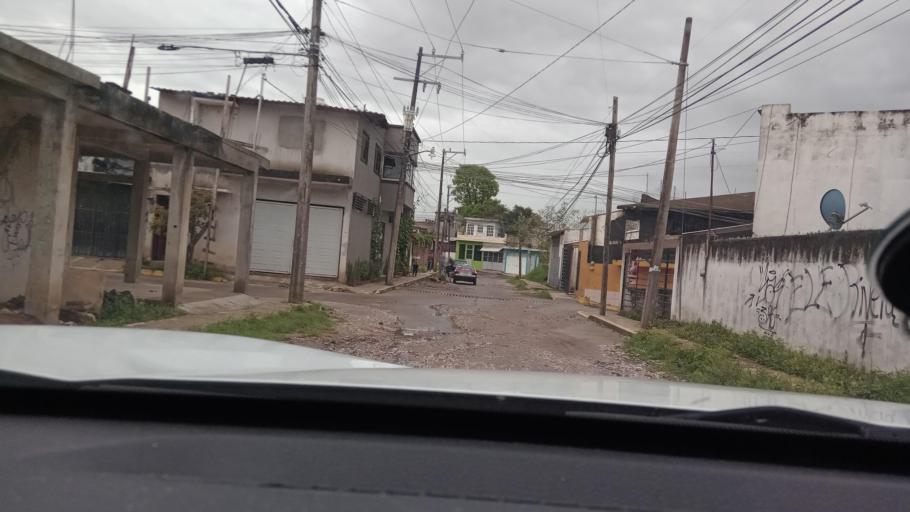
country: MX
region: Veracruz
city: Coatepec
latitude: 19.4439
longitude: -96.9686
